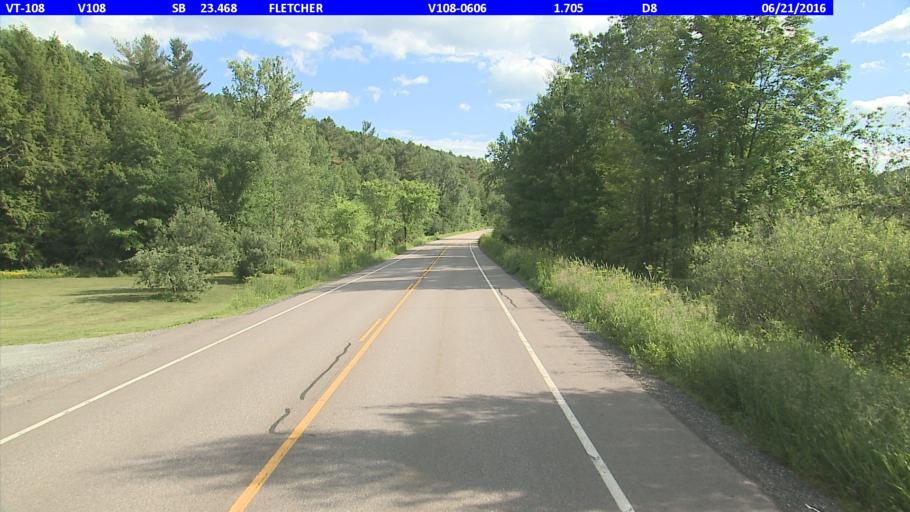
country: US
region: Vermont
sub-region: Lamoille County
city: Johnson
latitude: 44.7248
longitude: -72.8299
